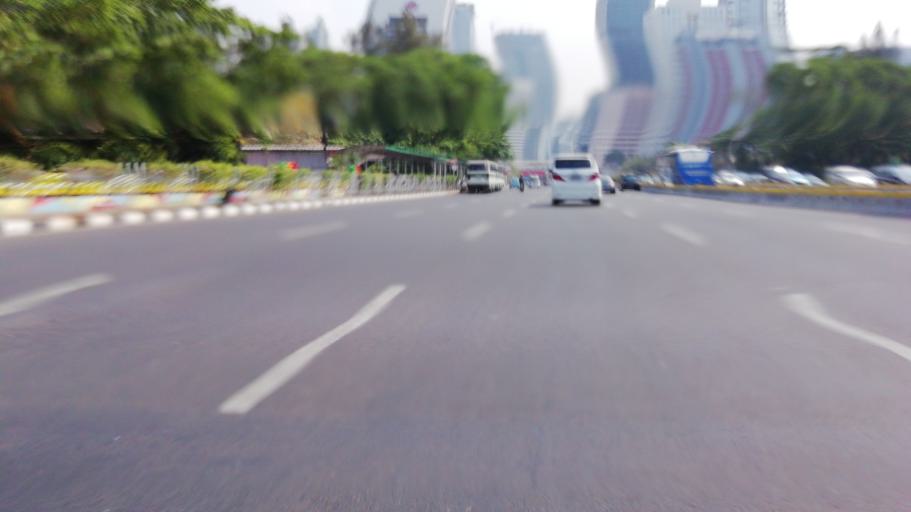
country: ID
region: Jakarta Raya
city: Jakarta
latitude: -6.2020
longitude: 106.8230
